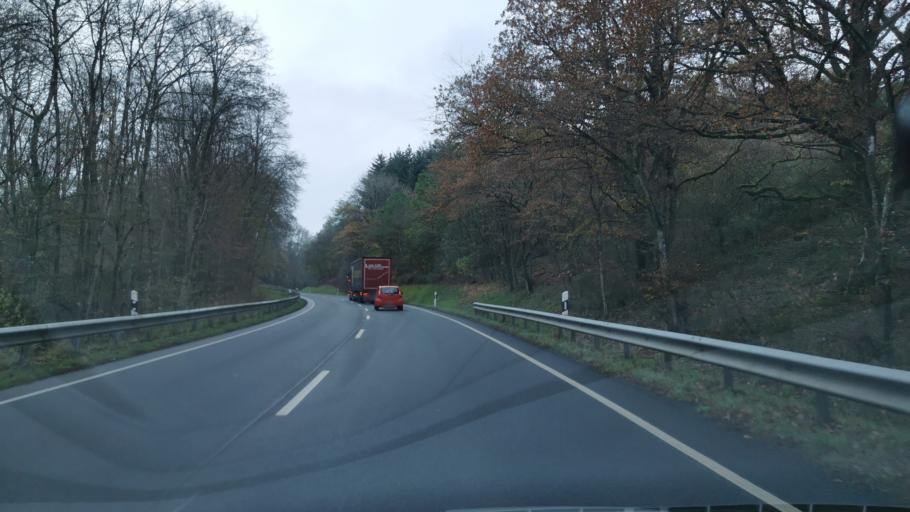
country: DE
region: Rheinland-Pfalz
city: Ediger-Eller
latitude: 50.1366
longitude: 7.1412
